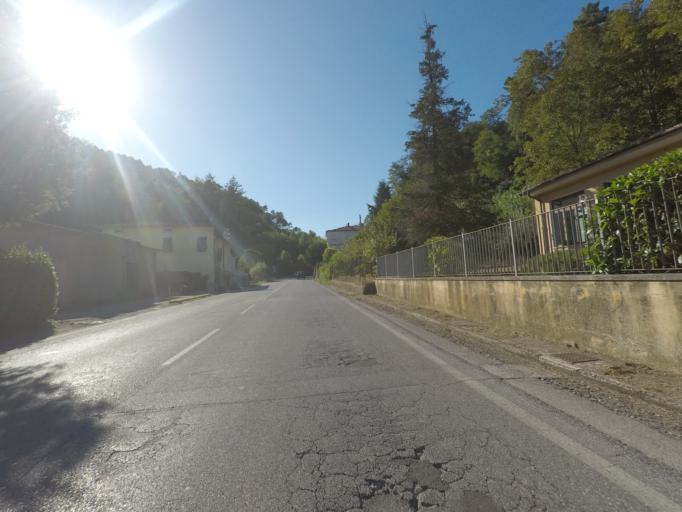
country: IT
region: Tuscany
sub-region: Provincia di Lucca
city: Massarosa
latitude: 43.9019
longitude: 10.3775
